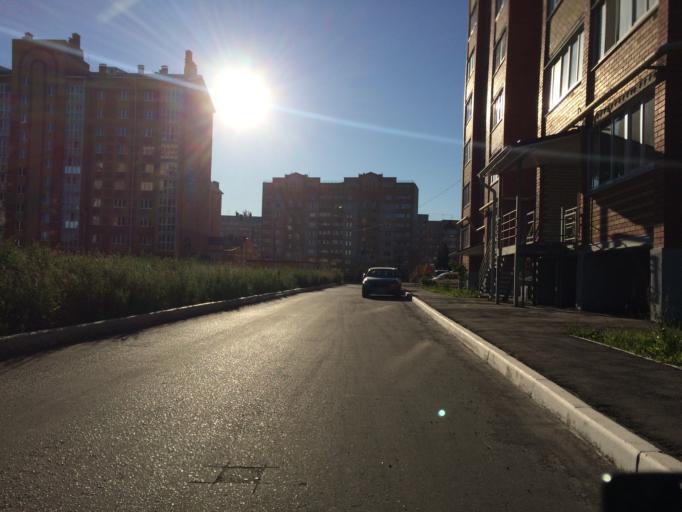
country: RU
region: Mariy-El
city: Medvedevo
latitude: 56.6458
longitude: 47.8314
